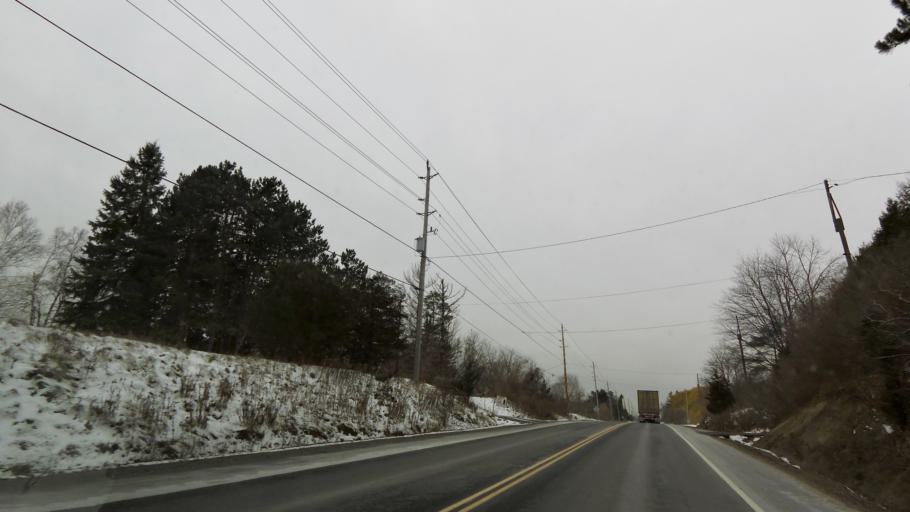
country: CA
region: Ontario
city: Vaughan
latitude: 43.9055
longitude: -79.6349
